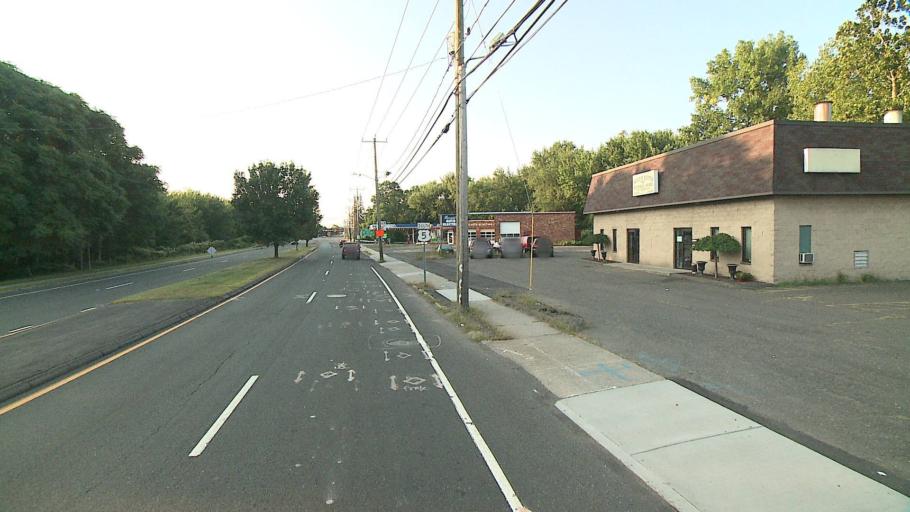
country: US
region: Connecticut
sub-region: Hartford County
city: Hartford
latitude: 41.7628
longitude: -72.6463
